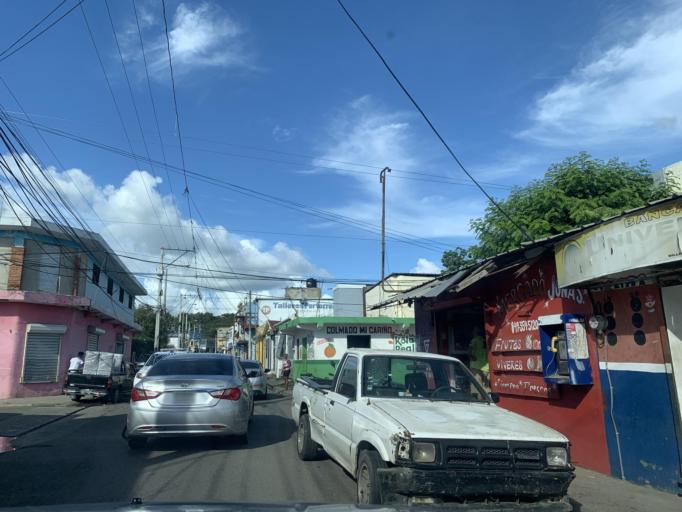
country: DO
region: Santiago
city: Santiago de los Caballeros
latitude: 19.4705
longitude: -70.7099
